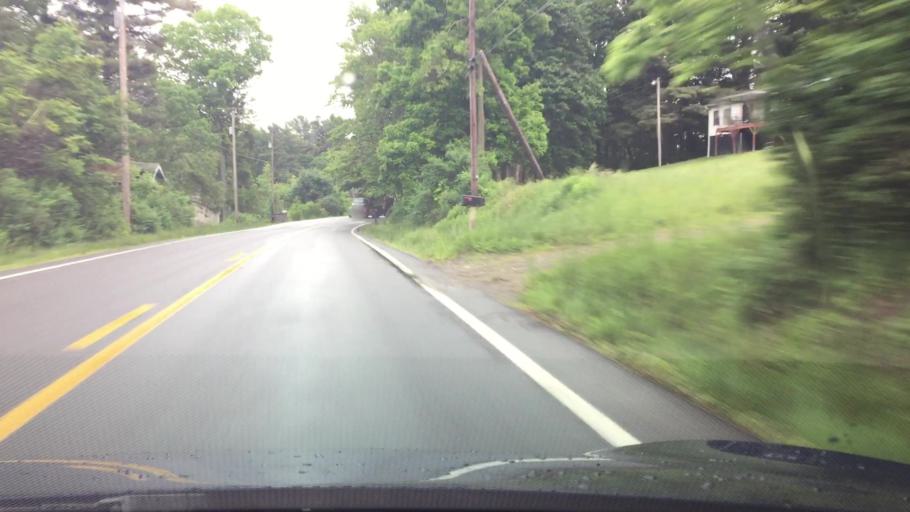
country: US
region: West Virginia
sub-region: Raleigh County
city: Shady Spring
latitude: 37.6929
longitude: -81.0691
